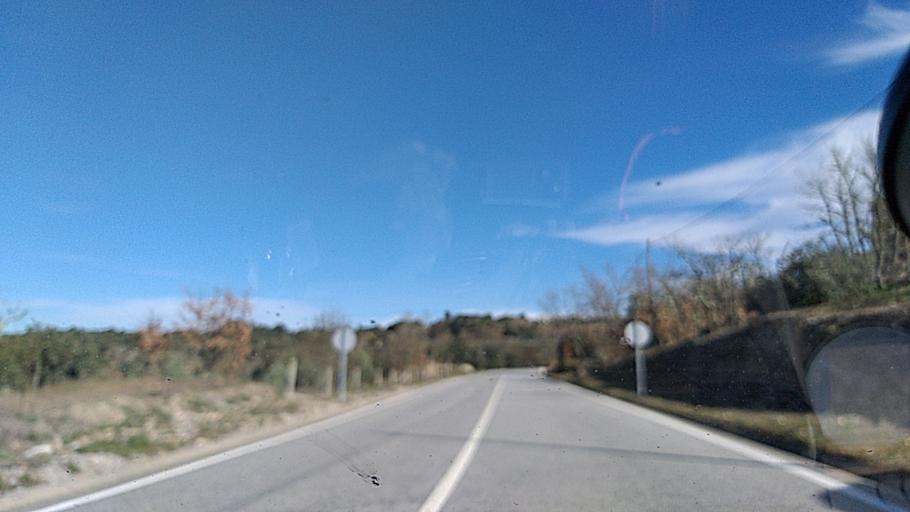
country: ES
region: Castille and Leon
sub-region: Provincia de Salamanca
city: Fuentes de Onoro
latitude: 40.6139
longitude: -6.8913
